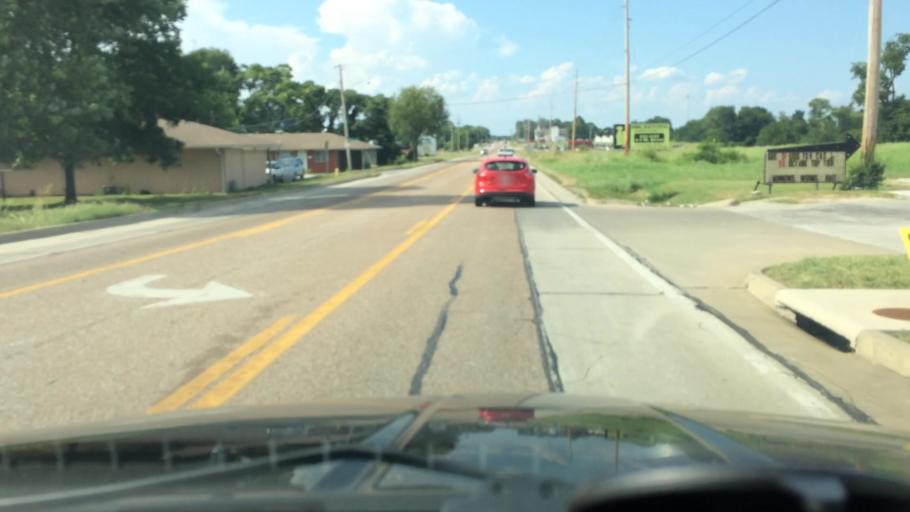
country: US
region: Missouri
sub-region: Greene County
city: Springfield
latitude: 37.2574
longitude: -93.2650
